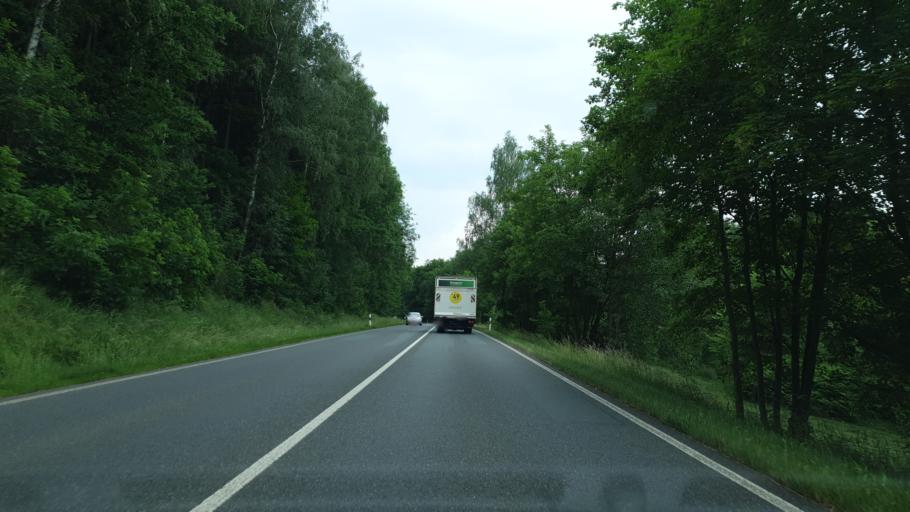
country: DE
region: Saxony
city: Lengenfeld
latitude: 50.5605
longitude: 12.3819
